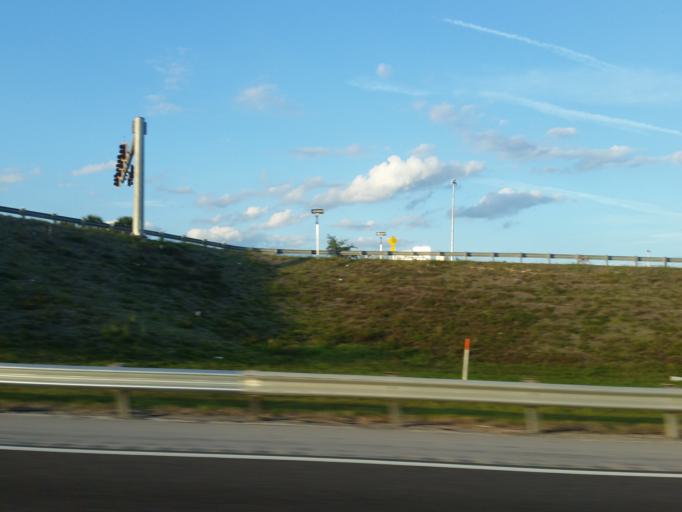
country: US
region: Florida
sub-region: Sarasota County
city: Nokomis
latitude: 27.1370
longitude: -82.4069
